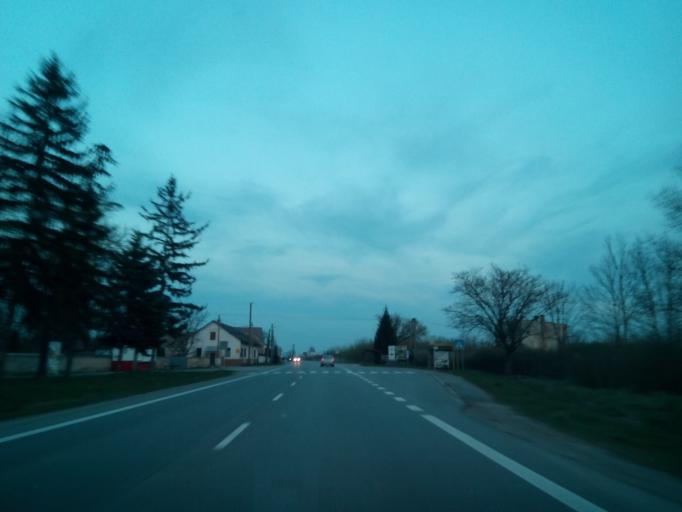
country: SK
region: Kosicky
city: Moldava nad Bodvou
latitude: 48.6076
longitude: 20.9499
